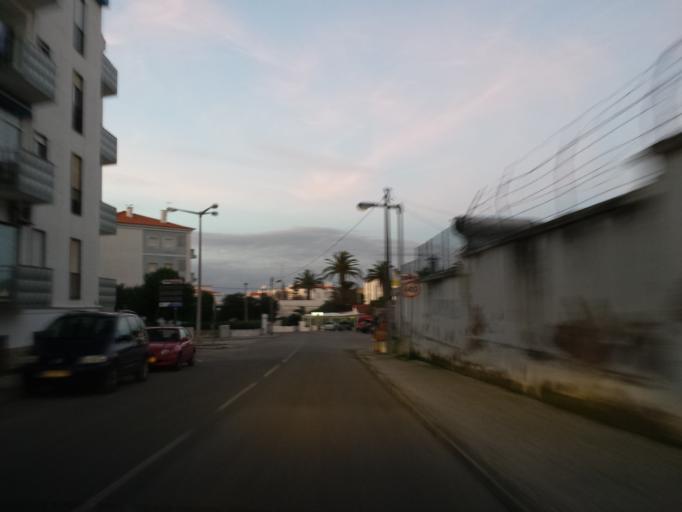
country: PT
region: Faro
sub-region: Lagos
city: Lagos
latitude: 37.0943
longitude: -8.6721
